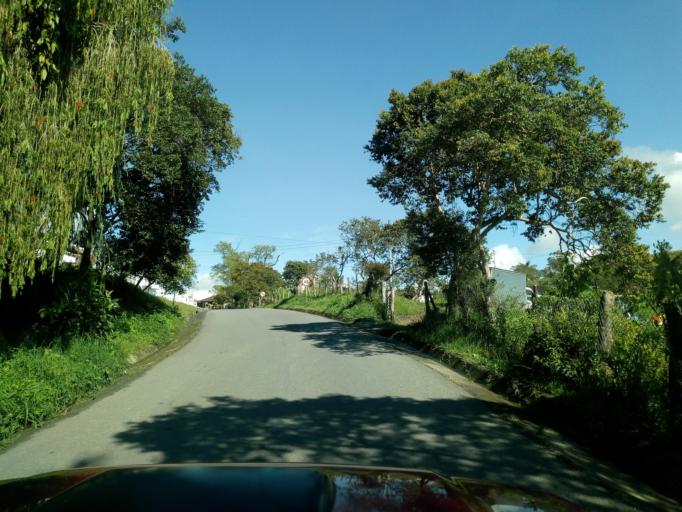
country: CO
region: Boyaca
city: Moniquira
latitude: 5.8703
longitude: -73.5536
